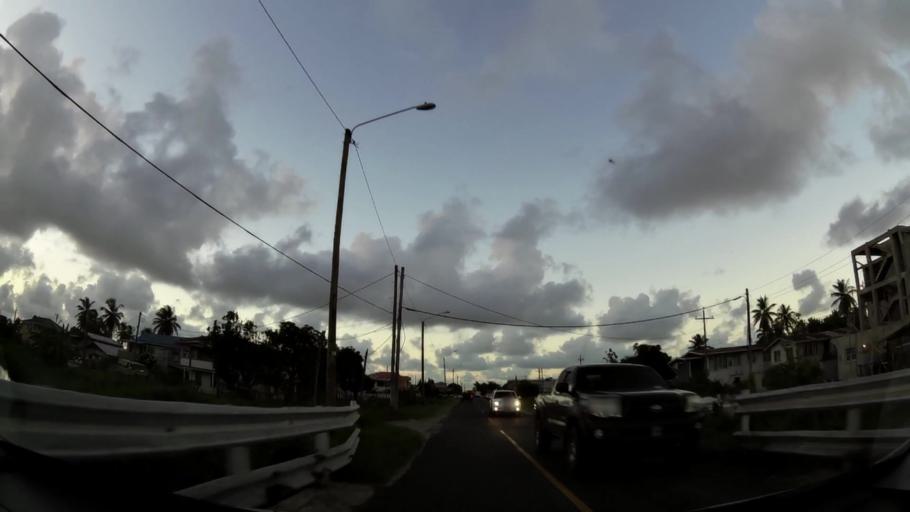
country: GY
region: Demerara-Mahaica
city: Georgetown
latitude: 6.8175
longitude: -58.0983
